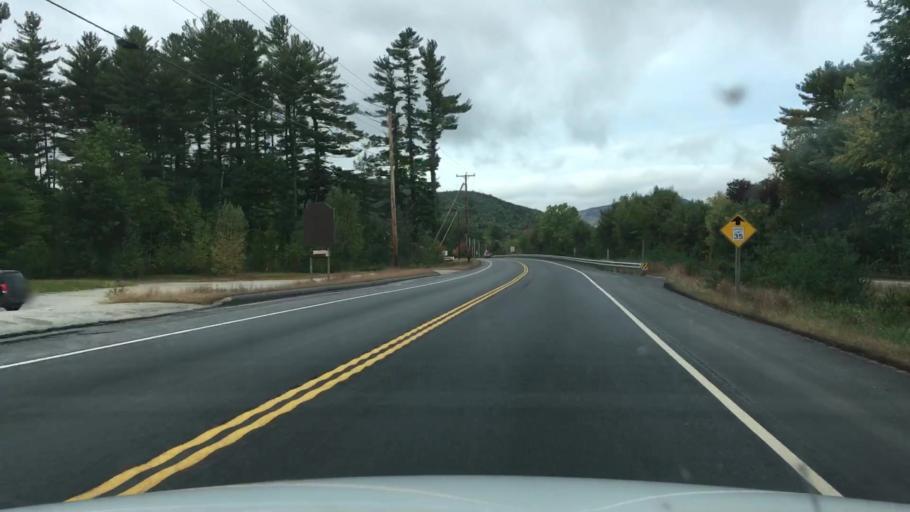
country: US
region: Maine
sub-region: Oxford County
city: Bethel
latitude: 44.4065
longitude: -70.8550
